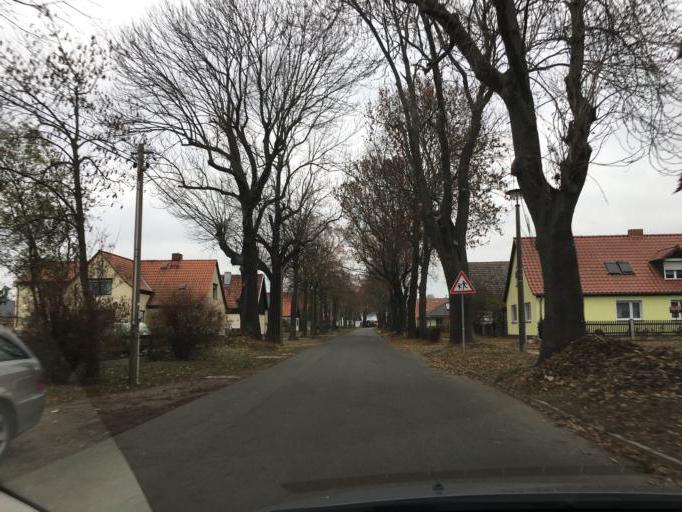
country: DE
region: Saxony-Anhalt
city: Wanzleben
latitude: 52.0376
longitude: 11.4545
